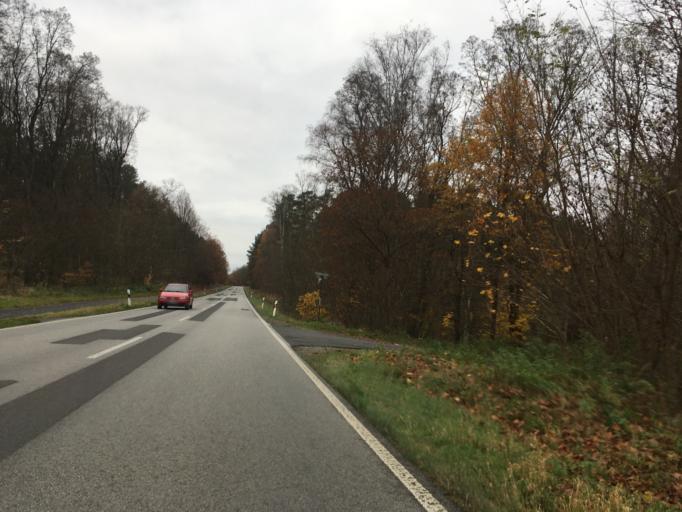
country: DE
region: Brandenburg
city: Mullrose
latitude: 52.2227
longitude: 14.4426
